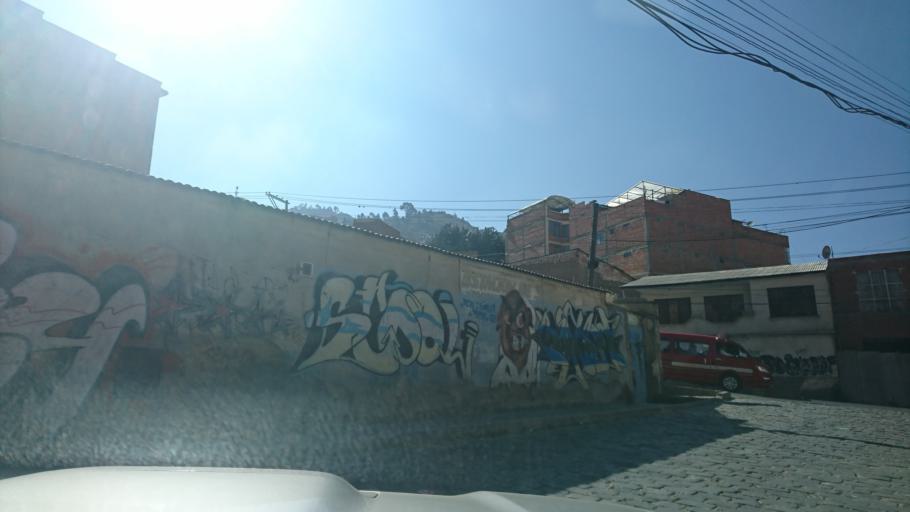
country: BO
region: La Paz
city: La Paz
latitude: -16.4861
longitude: -68.1180
